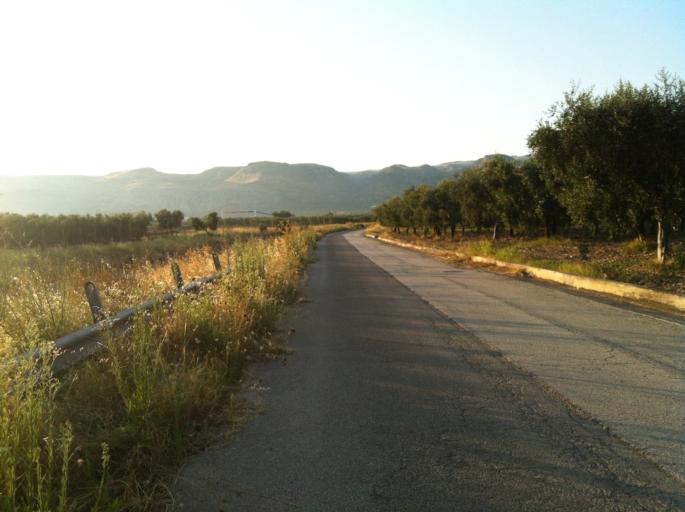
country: IT
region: Apulia
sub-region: Provincia di Foggia
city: Manfredonia
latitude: 41.6492
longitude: 15.9559
